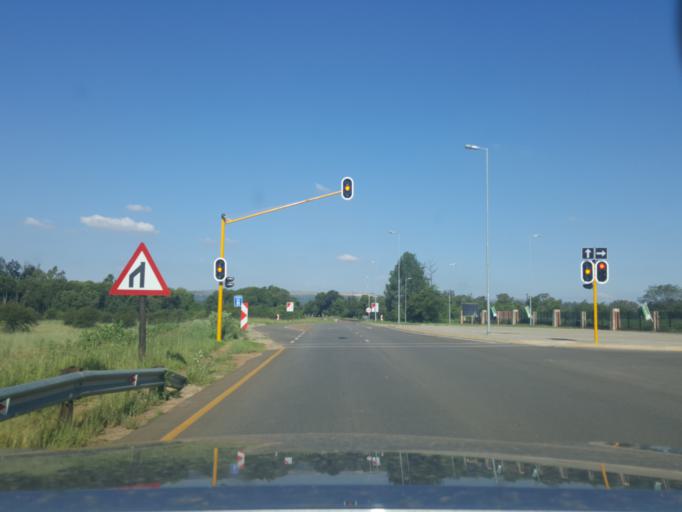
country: ZA
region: Gauteng
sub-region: City of Tshwane Metropolitan Municipality
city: Cullinan
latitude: -25.7542
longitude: 28.3778
